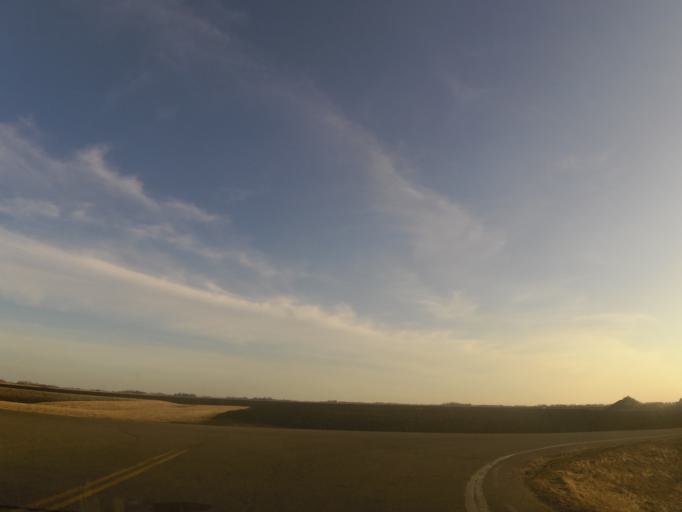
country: US
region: North Dakota
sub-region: Grand Forks County
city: Grand Forks
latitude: 47.8604
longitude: -97.0292
